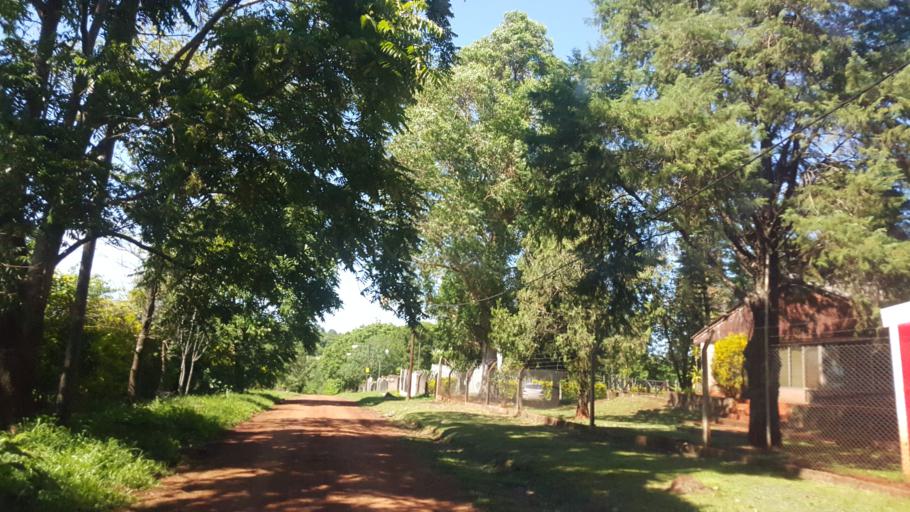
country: AR
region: Misiones
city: Garupa
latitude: -27.4876
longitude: -55.8599
